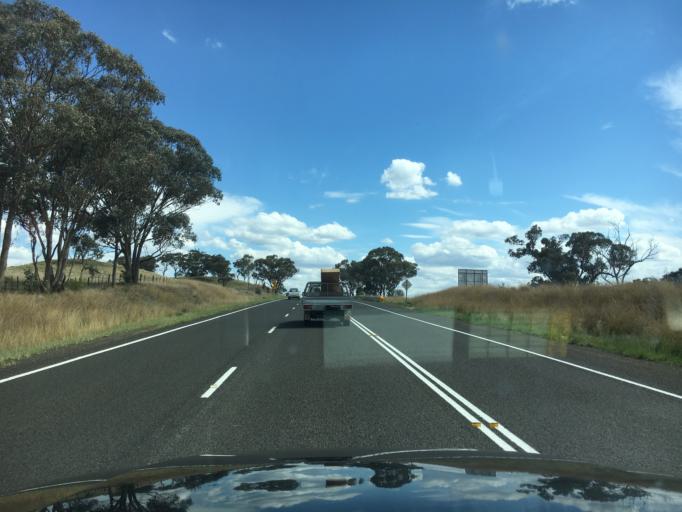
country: AU
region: New South Wales
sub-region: Liverpool Plains
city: Quirindi
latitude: -31.4991
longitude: 150.8644
